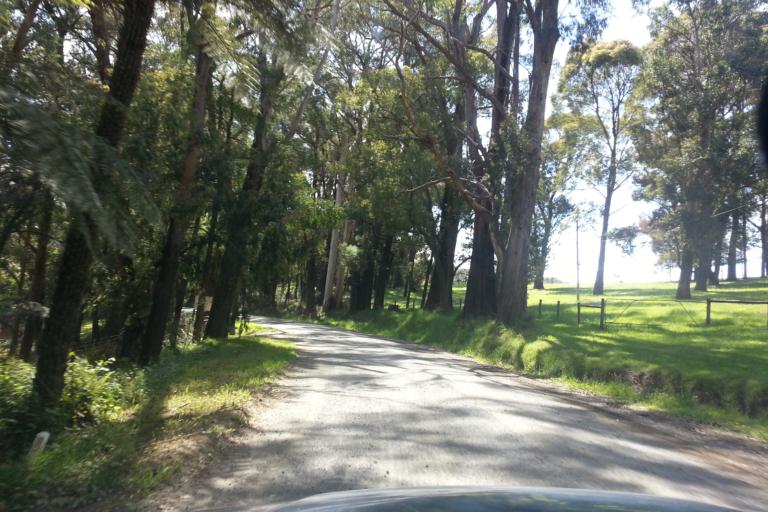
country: AU
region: Victoria
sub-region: Cardinia
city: Gembrook
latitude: -37.9529
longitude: 145.5739
